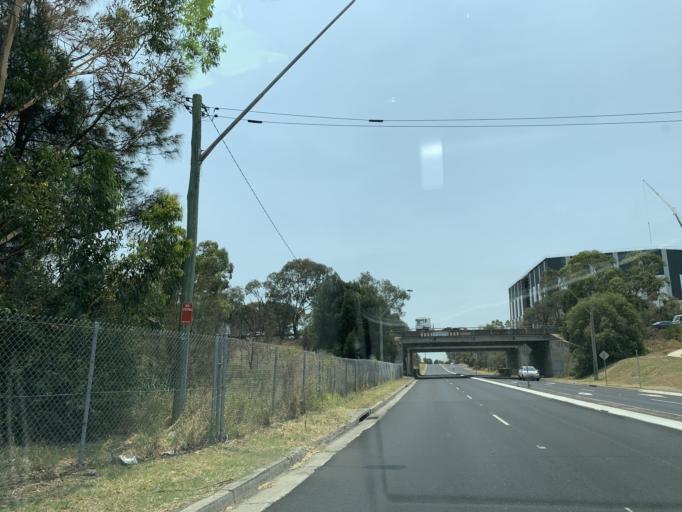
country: AU
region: New South Wales
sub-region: Blacktown
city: Doonside
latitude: -33.8019
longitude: 150.8699
